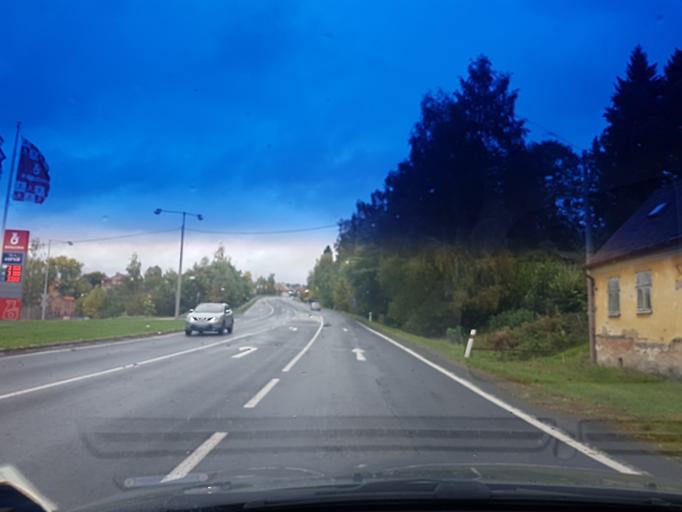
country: CZ
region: Karlovarsky
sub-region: Okres Cheb
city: Cheb
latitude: 50.0726
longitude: 12.3615
